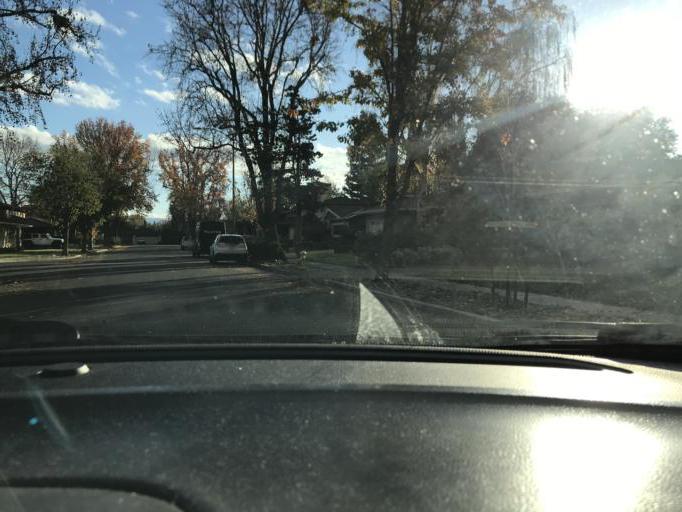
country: US
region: California
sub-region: Santa Clara County
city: Campbell
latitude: 37.2920
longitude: -121.9218
